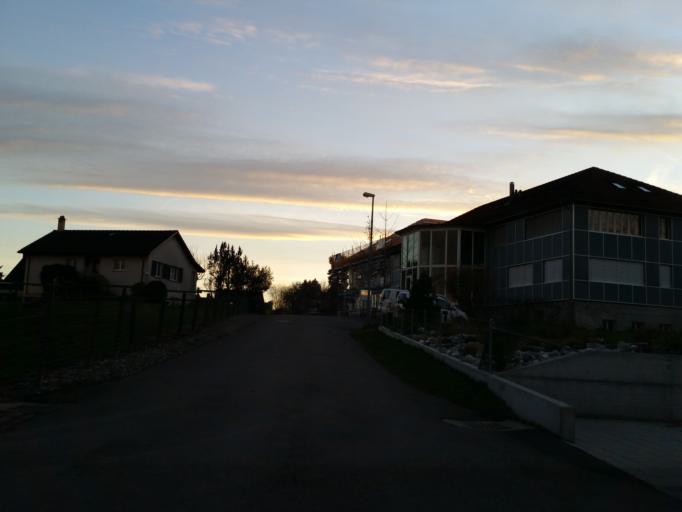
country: CH
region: Thurgau
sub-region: Arbon District
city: Uttwil
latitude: 47.5928
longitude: 9.3189
